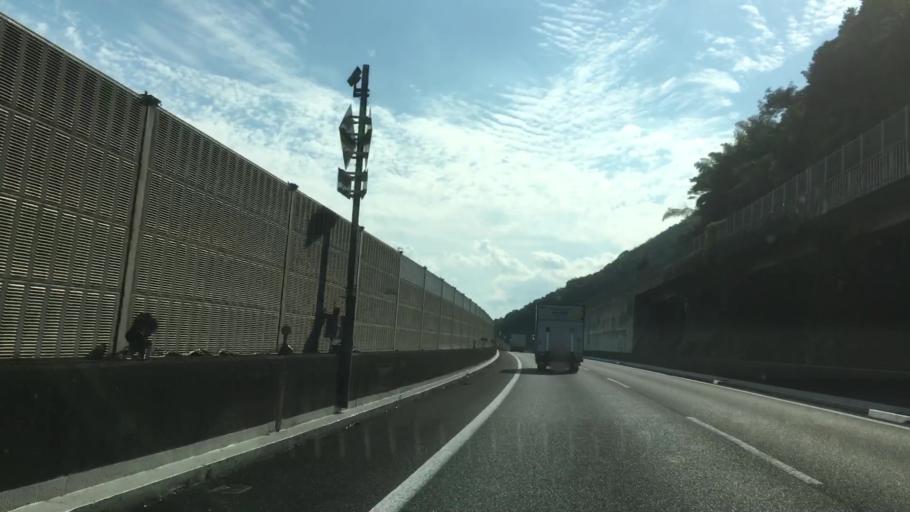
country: JP
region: Yamaguchi
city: Otake
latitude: 34.2230
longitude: 132.2013
